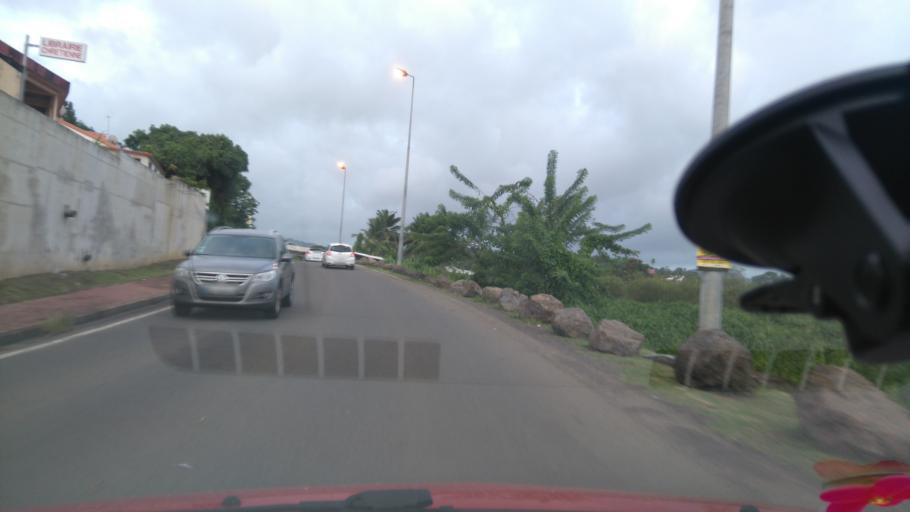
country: MQ
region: Martinique
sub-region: Martinique
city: Ducos
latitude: 14.5547
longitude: -60.9725
